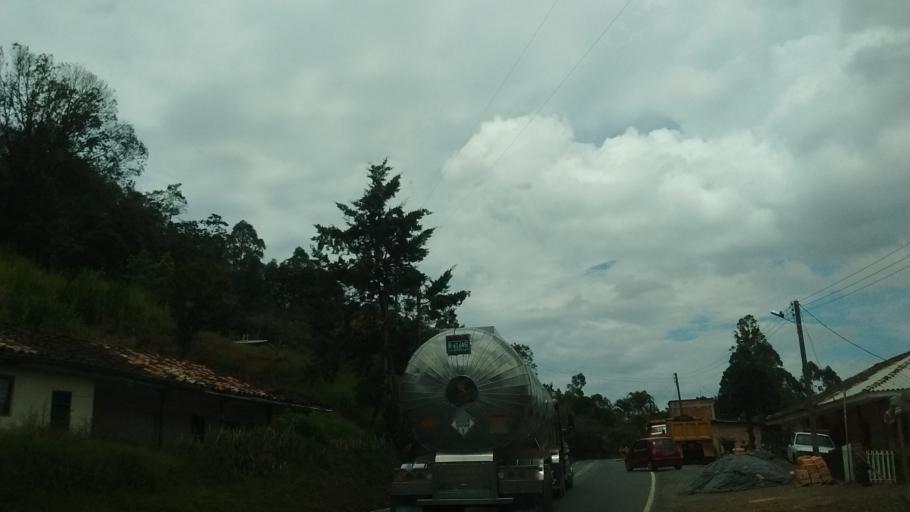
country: CO
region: Cauca
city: Rosas
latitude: 2.3060
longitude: -76.6955
